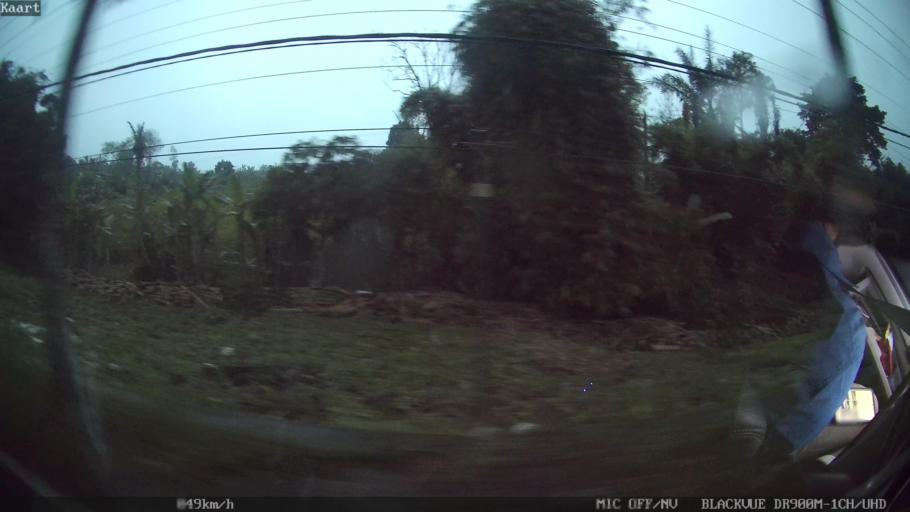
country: ID
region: Bali
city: Banjar Taro Kelod
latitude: -8.3151
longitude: 115.3006
